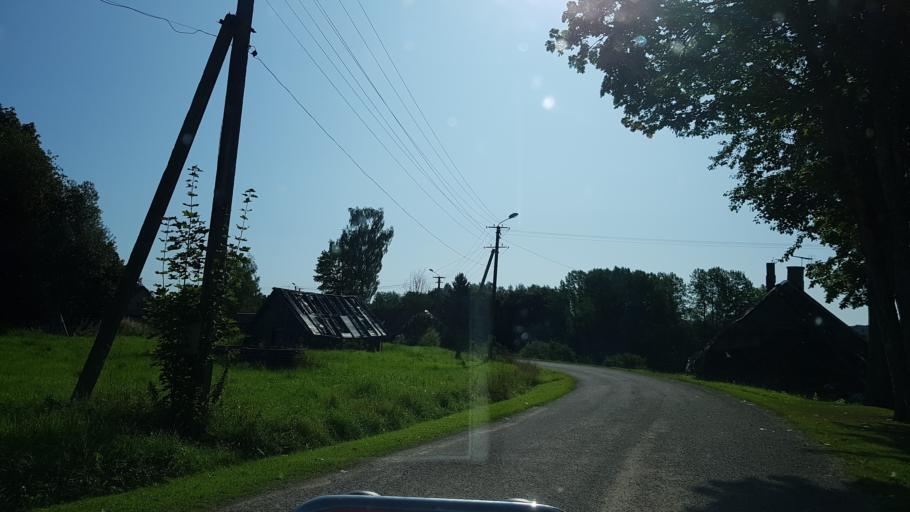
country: EE
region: Vorumaa
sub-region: Voru linn
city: Voru
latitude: 57.7333
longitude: 26.9214
